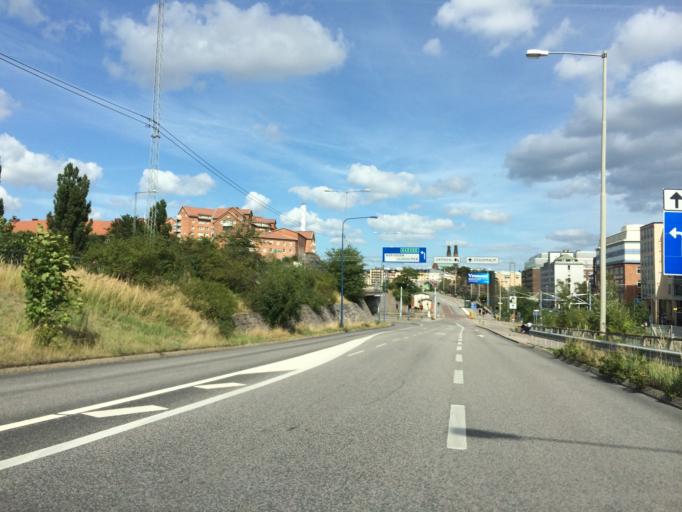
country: SE
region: Stockholm
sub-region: Stockholms Kommun
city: Arsta
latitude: 59.3089
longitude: 18.0259
